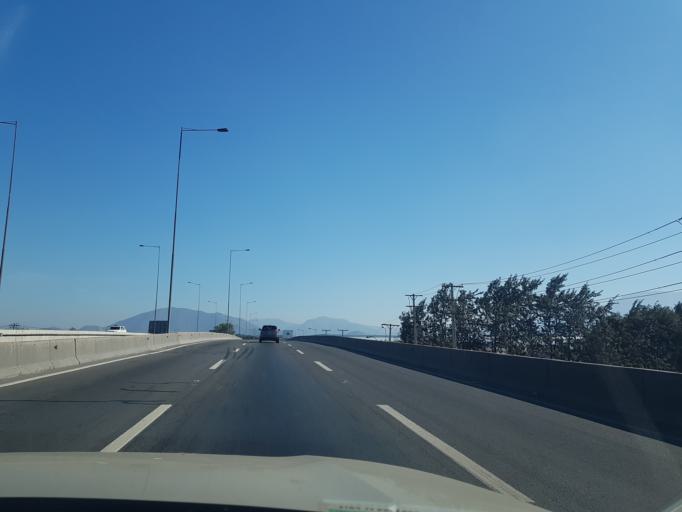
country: CL
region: Santiago Metropolitan
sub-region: Provincia de Santiago
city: Lo Prado
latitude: -33.3937
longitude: -70.7689
